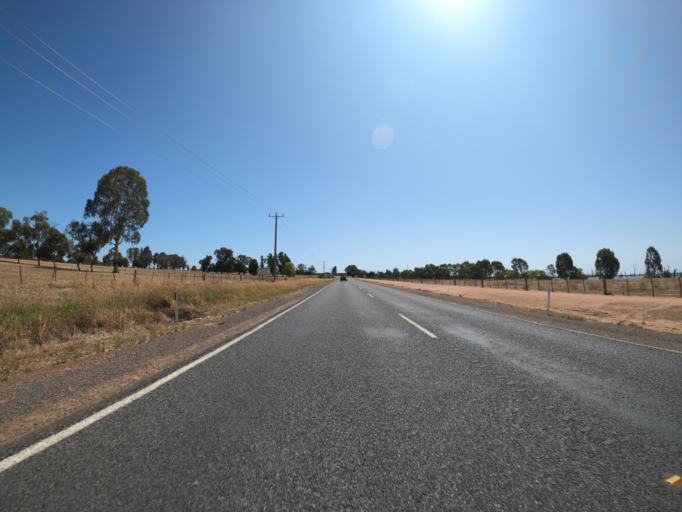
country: AU
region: Victoria
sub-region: Moira
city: Yarrawonga
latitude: -36.0268
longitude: 146.0839
